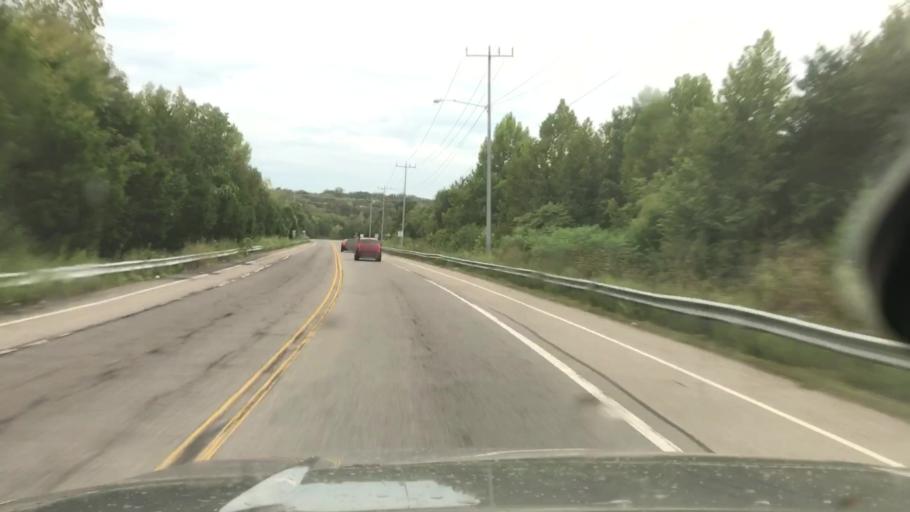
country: US
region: Tennessee
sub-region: Rutherford County
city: La Vergne
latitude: 36.1146
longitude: -86.6314
